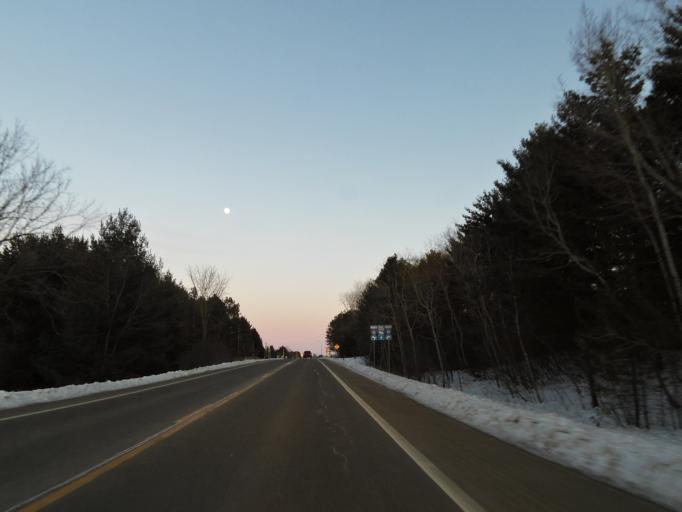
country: US
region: Minnesota
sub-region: Washington County
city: Grant
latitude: 45.0795
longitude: -92.8677
